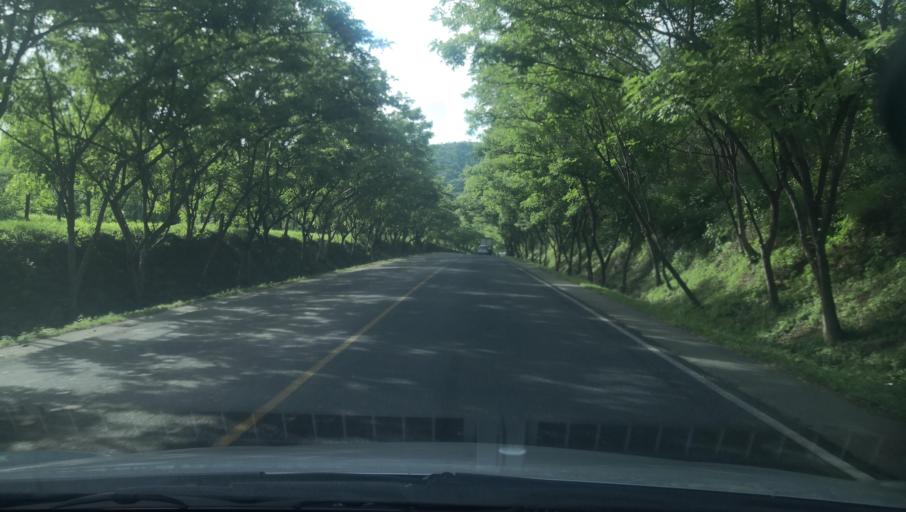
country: NI
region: Madriz
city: Totogalpa
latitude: 13.5810
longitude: -86.4777
